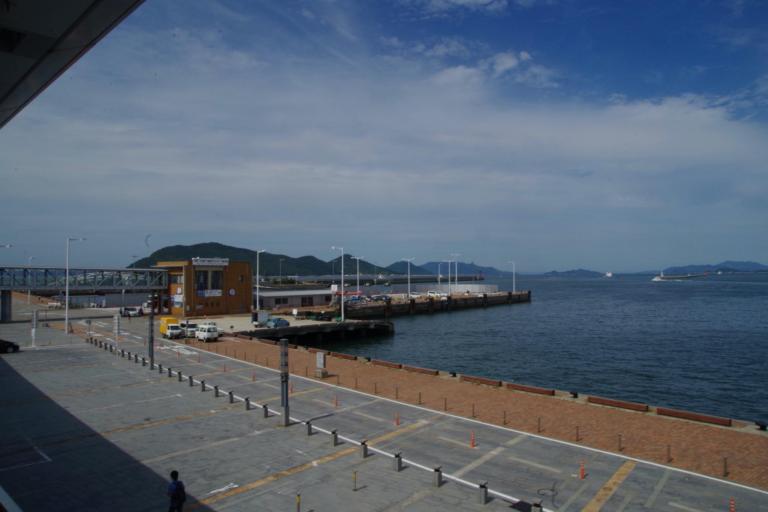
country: JP
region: Kagawa
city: Takamatsu-shi
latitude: 34.3531
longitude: 134.0488
